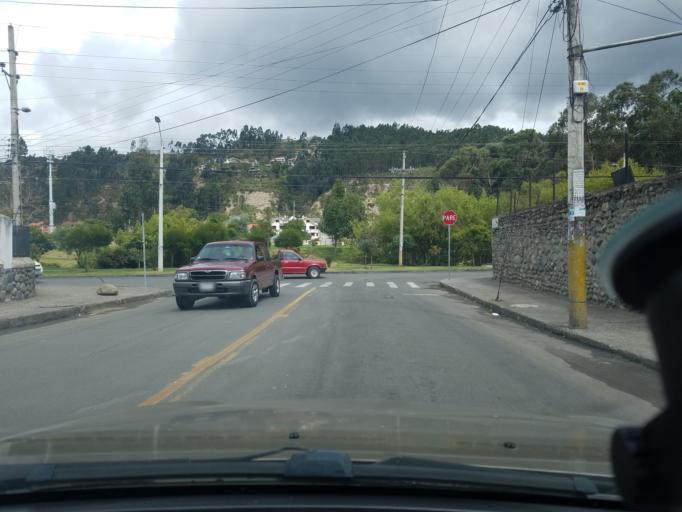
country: EC
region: Azuay
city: Cuenca
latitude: -2.9070
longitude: -78.9846
